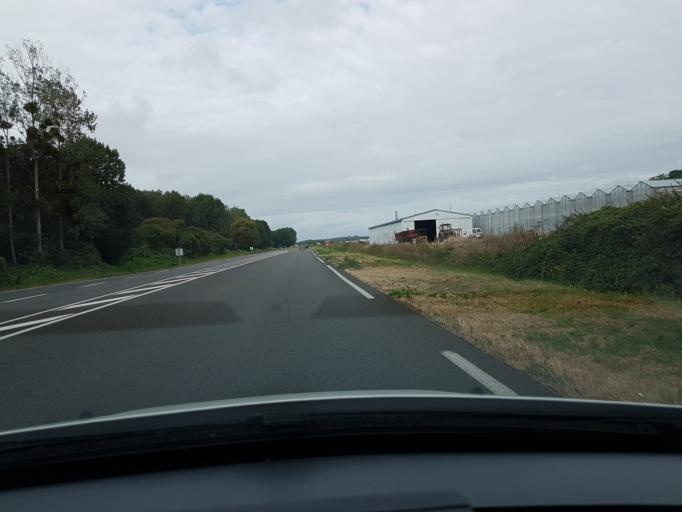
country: FR
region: Centre
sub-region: Departement d'Indre-et-Loire
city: Saint-Martin-le-Beau
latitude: 47.3562
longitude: 0.8952
